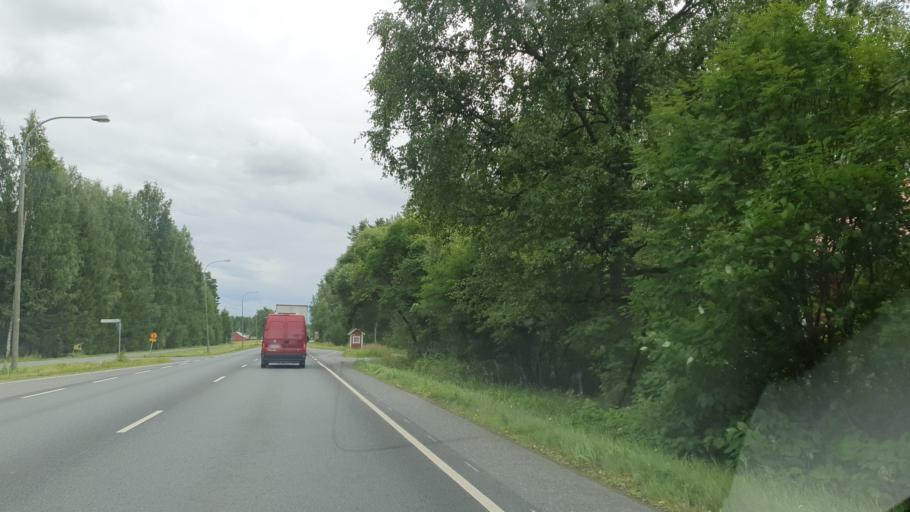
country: FI
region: Northern Savo
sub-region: Ylae-Savo
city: Lapinlahti
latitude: 63.4661
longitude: 27.3078
